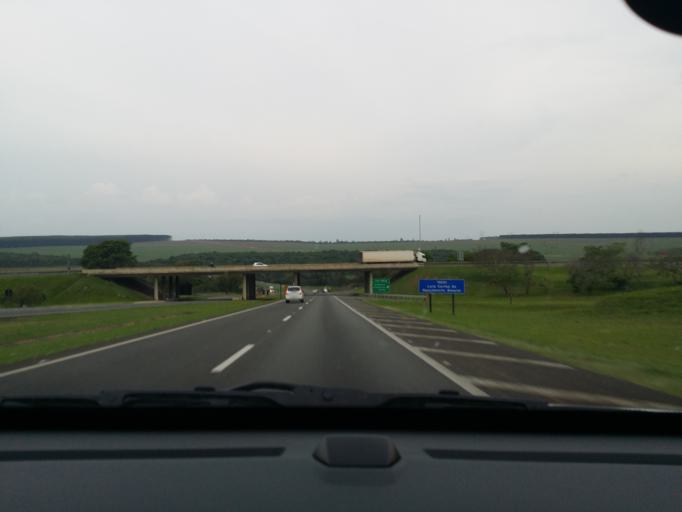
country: BR
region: Sao Paulo
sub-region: Itirapina
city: Itirapina
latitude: -22.2144
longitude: -47.7673
